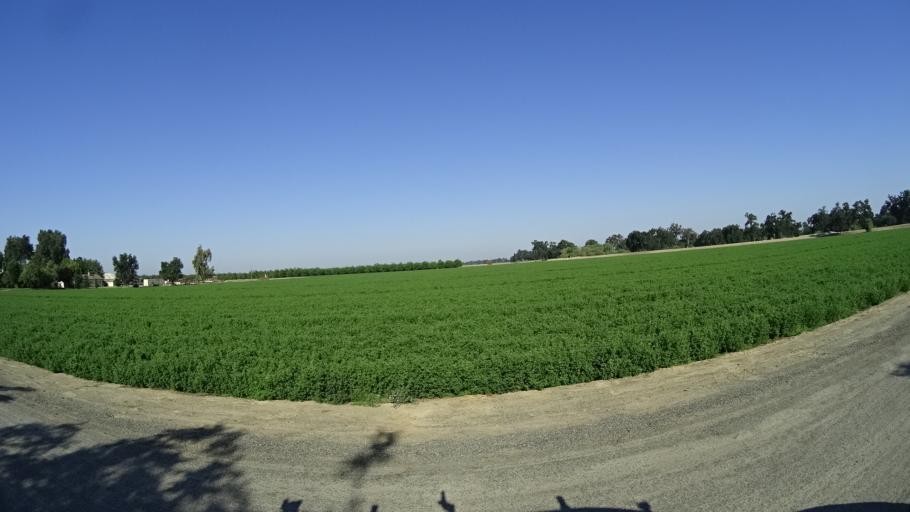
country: US
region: California
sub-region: Fresno County
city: Laton
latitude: 36.4154
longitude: -119.7132
